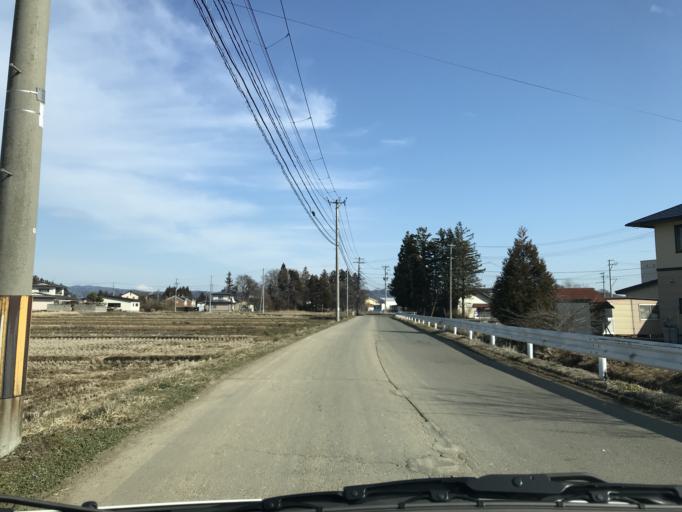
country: JP
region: Iwate
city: Kitakami
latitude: 39.3005
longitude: 141.0947
